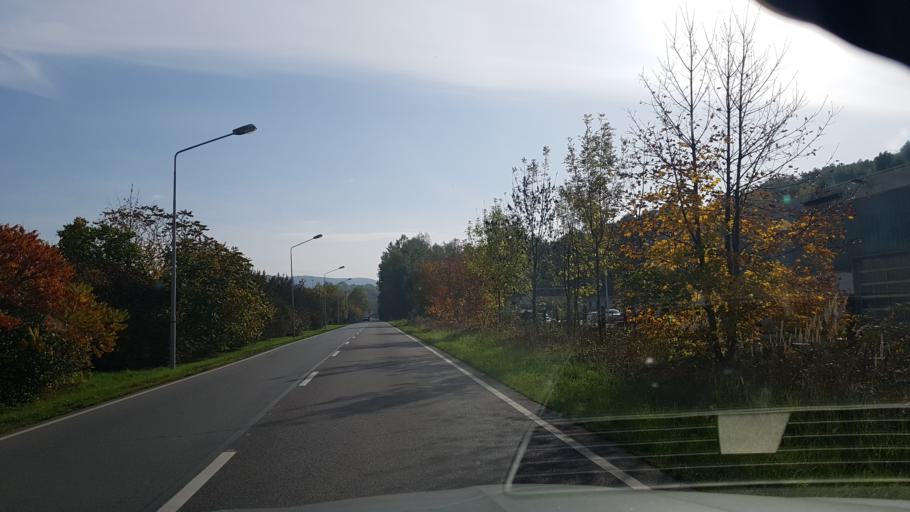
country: DE
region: Saxony
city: Dohma
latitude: 50.9283
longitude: 13.9544
